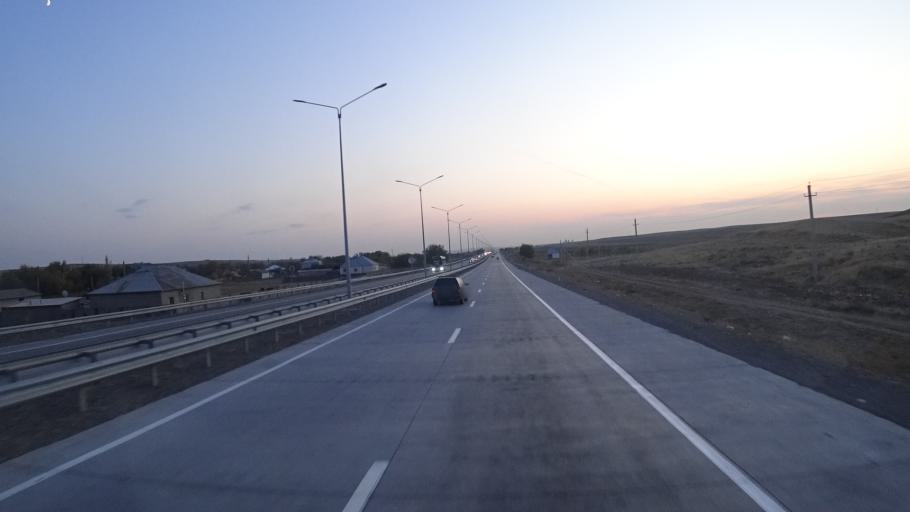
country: KZ
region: Ongtustik Qazaqstan
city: Qazyqurt
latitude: 41.8933
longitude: 69.4502
